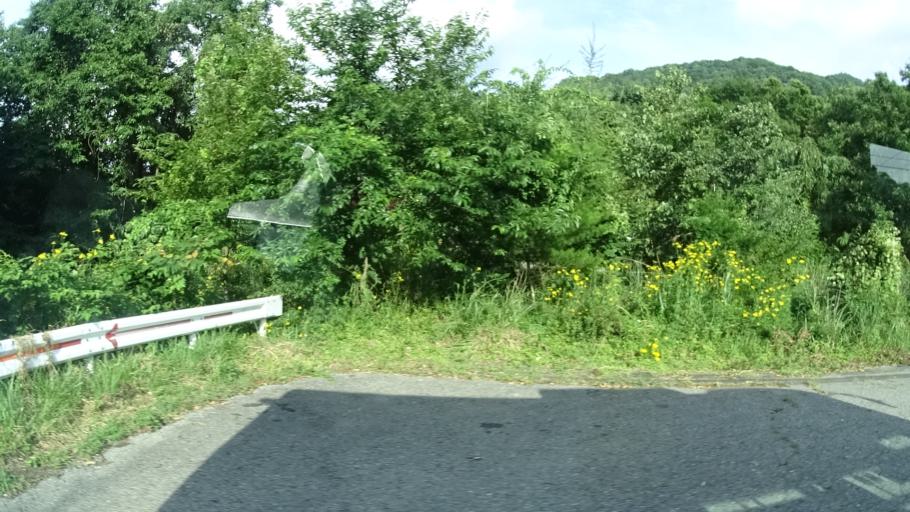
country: JP
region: Tochigi
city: Nikko
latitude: 36.6607
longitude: 139.4594
